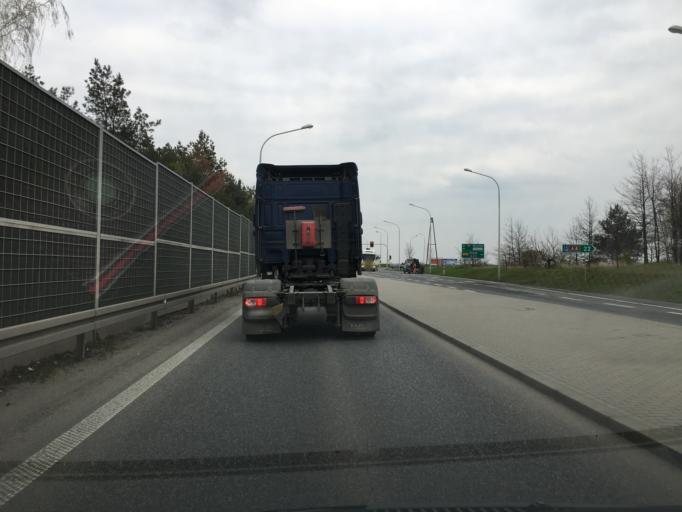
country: PL
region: Lower Silesian Voivodeship
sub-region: Powiat sredzki
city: Sroda Slaska
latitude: 51.1596
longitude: 16.6044
